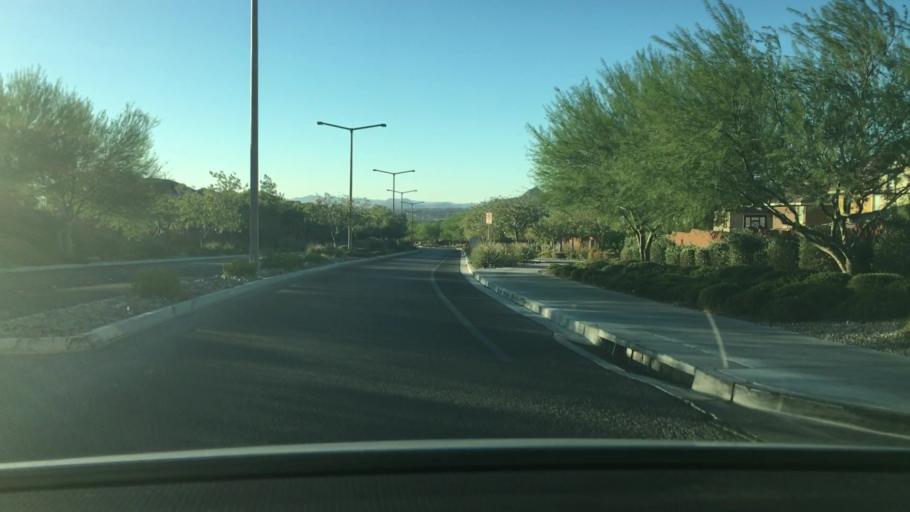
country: US
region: Nevada
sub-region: Clark County
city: Summerlin South
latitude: 36.0897
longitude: -115.3247
